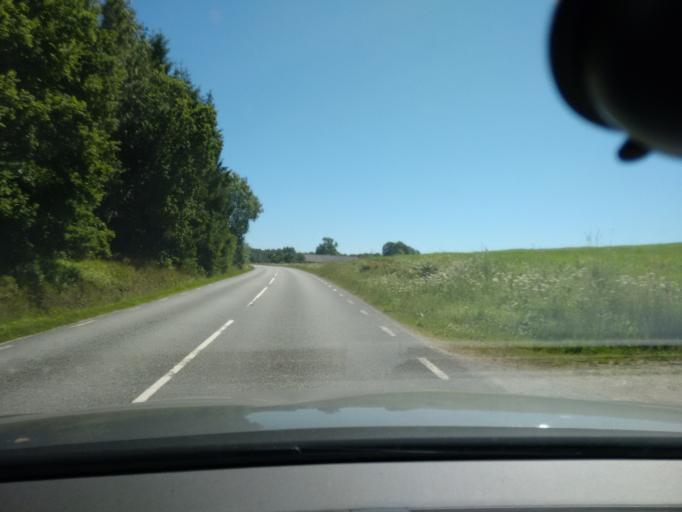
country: SE
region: Skane
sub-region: Kristianstads Kommun
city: Degeberga
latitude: 55.7817
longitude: 13.8797
